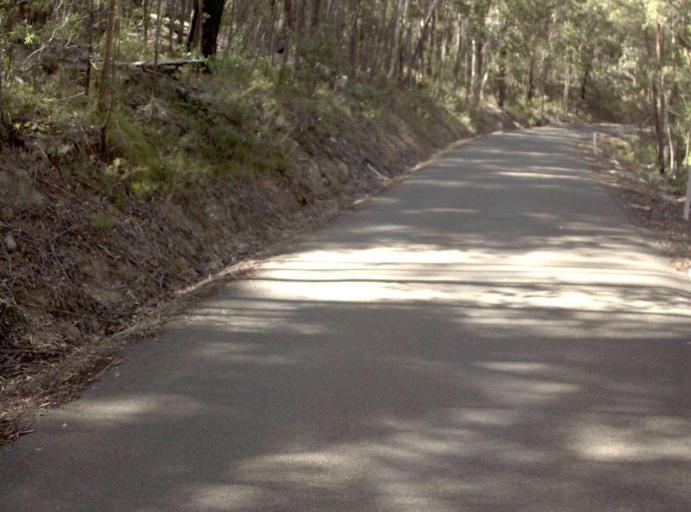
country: AU
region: Victoria
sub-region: East Gippsland
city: Lakes Entrance
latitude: -37.4460
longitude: 148.1277
